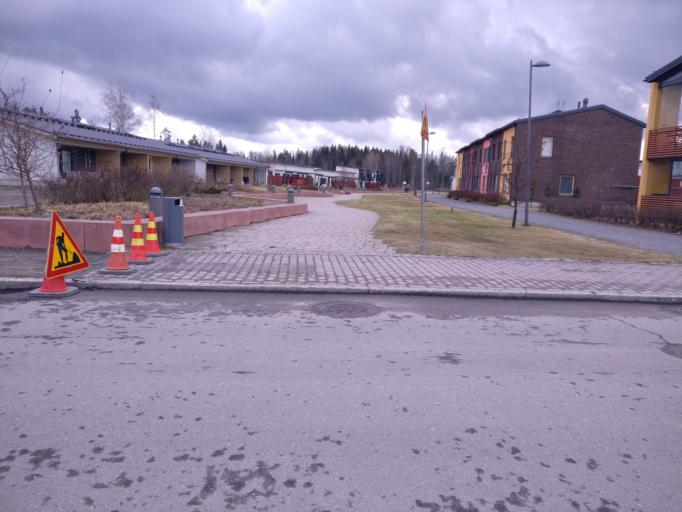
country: FI
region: Pirkanmaa
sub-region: Tampere
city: Tampere
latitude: 61.4387
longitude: 23.8138
